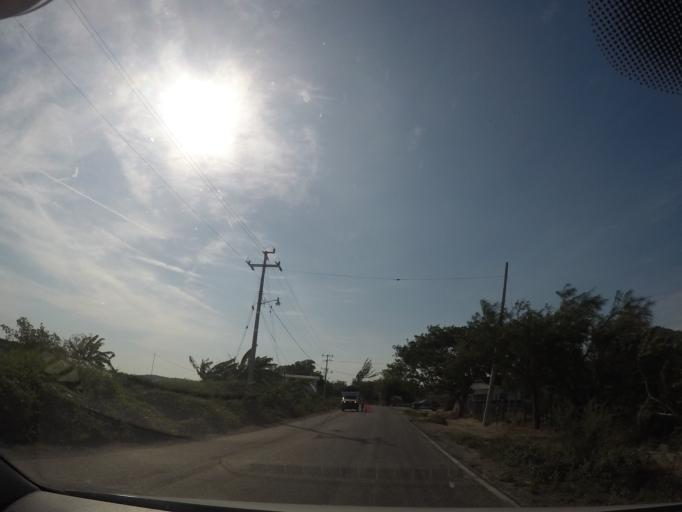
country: MX
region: Oaxaca
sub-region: Salina Cruz
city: Salina Cruz
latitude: 16.2208
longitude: -95.1312
